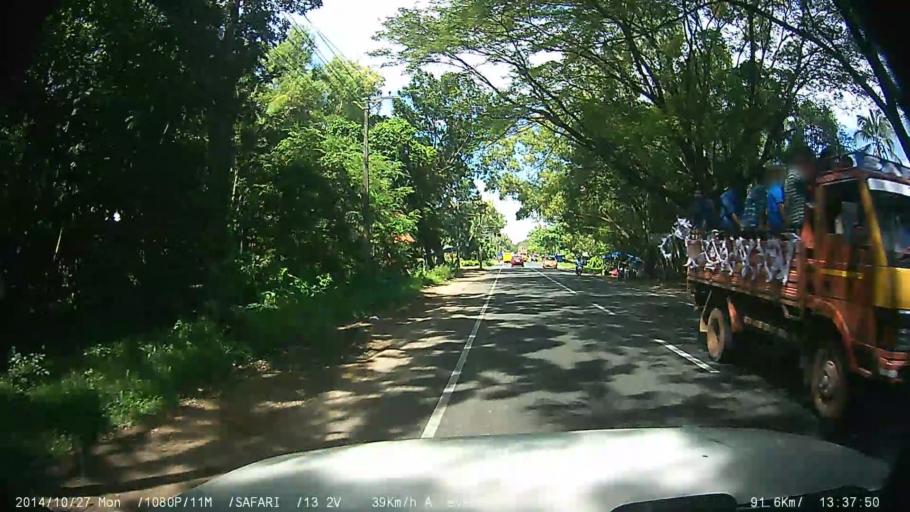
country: IN
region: Kerala
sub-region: Alappuzha
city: Shertallai
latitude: 9.6140
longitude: 76.3304
